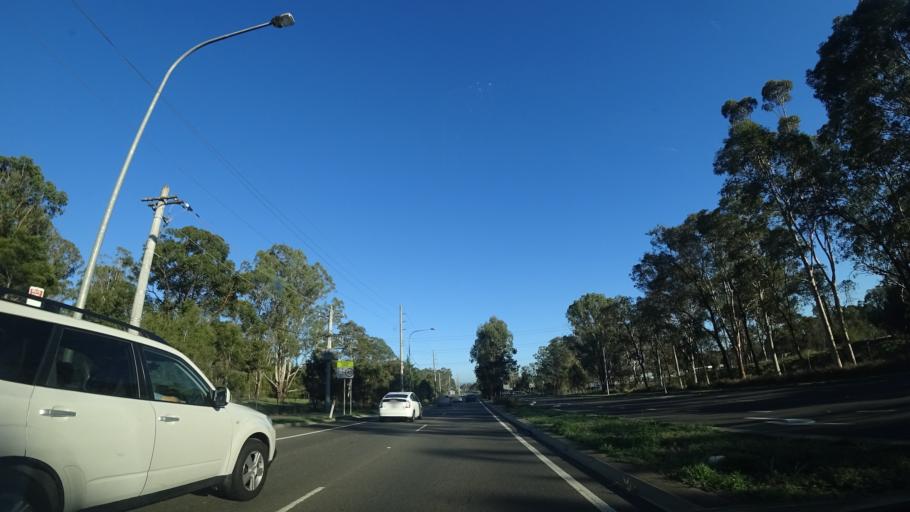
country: AU
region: New South Wales
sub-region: Blacktown
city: Riverstone
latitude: -33.6458
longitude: 150.8581
